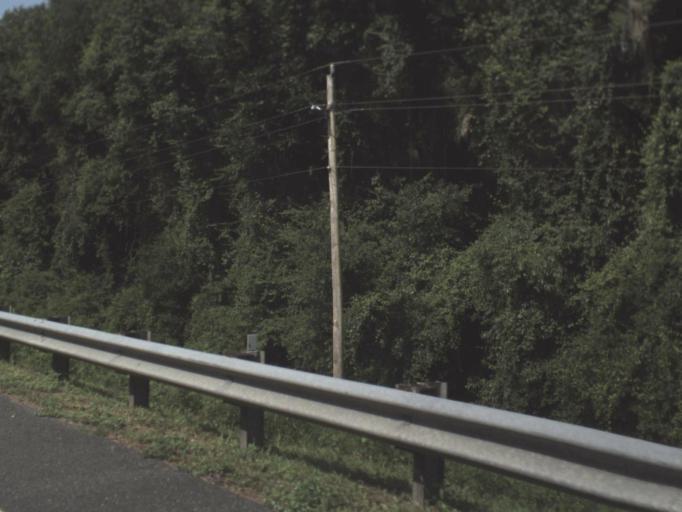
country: US
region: Florida
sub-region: Lafayette County
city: Mayo
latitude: 30.1108
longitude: -83.1707
